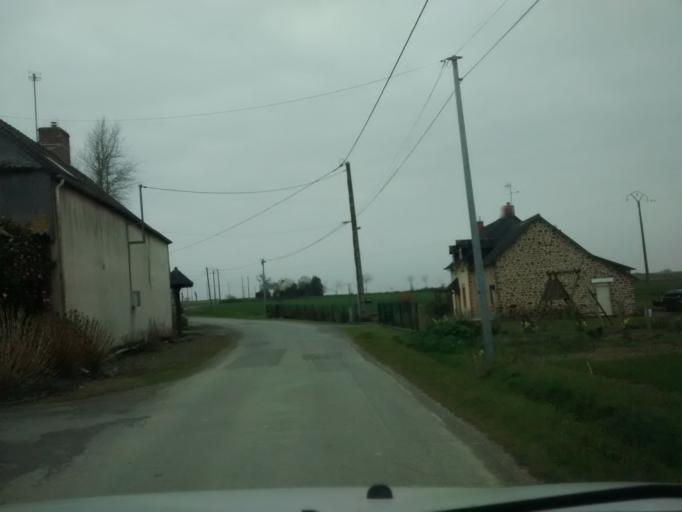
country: FR
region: Brittany
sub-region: Departement d'Ille-et-Vilaine
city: Bazouges-la-Perouse
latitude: 48.3879
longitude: -1.5837
